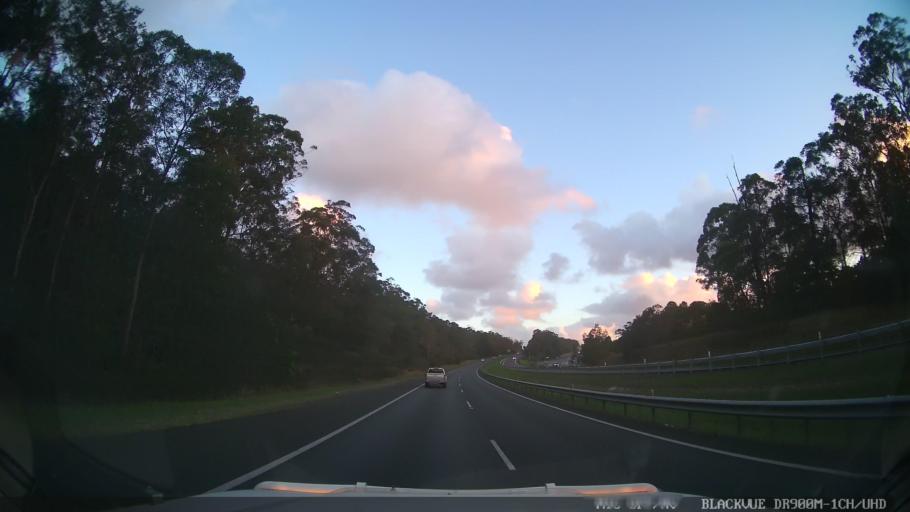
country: AU
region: Queensland
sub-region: Sunshine Coast
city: Yandina
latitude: -26.5848
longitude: 152.9667
